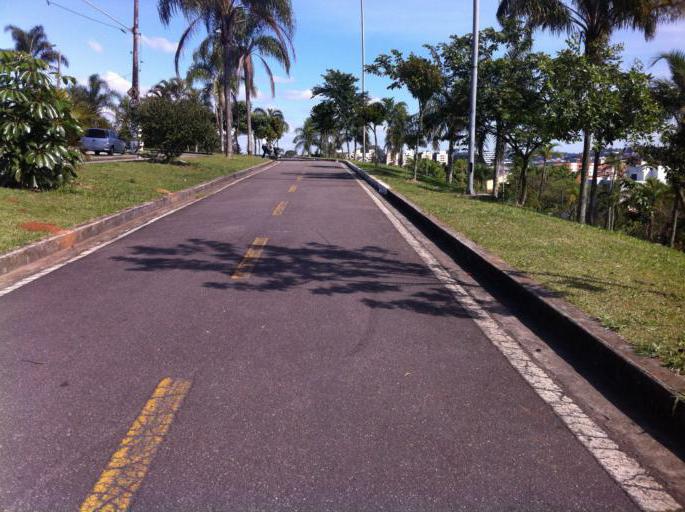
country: BR
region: Sao Paulo
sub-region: Sao Bernardo Do Campo
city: Sao Bernardo do Campo
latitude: -23.7305
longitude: -46.5637
